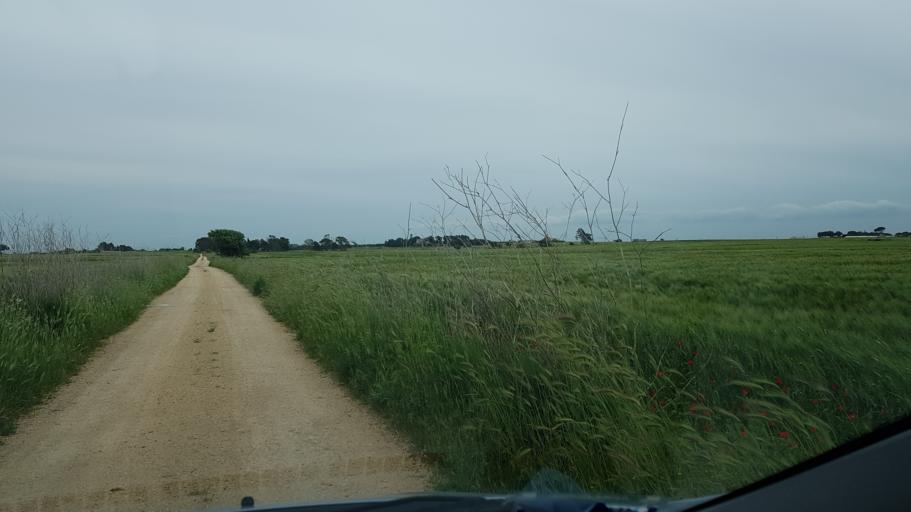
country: IT
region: Apulia
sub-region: Provincia di Brindisi
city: Brindisi
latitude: 40.6560
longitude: 17.8816
